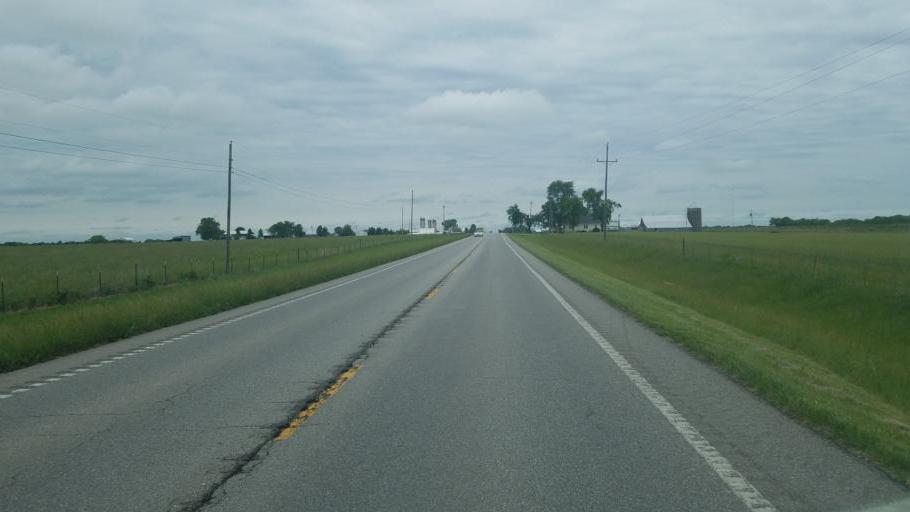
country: US
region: Missouri
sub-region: Morgan County
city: Versailles
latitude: 38.4727
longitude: -92.8087
